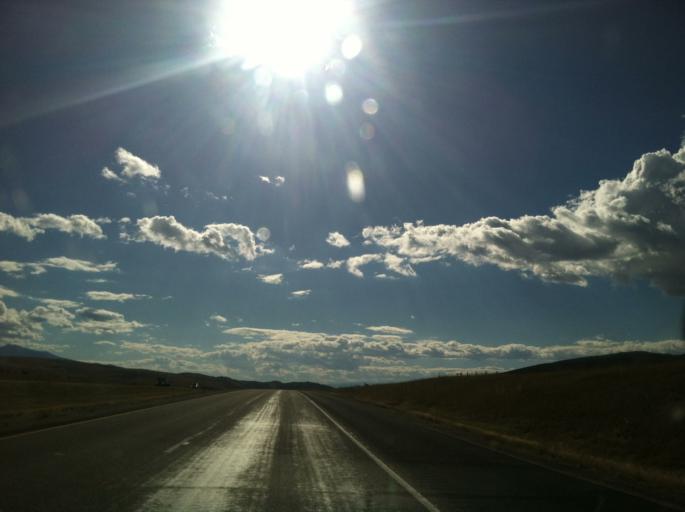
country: US
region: Montana
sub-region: Jefferson County
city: Whitehall
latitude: 45.8905
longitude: -111.8564
